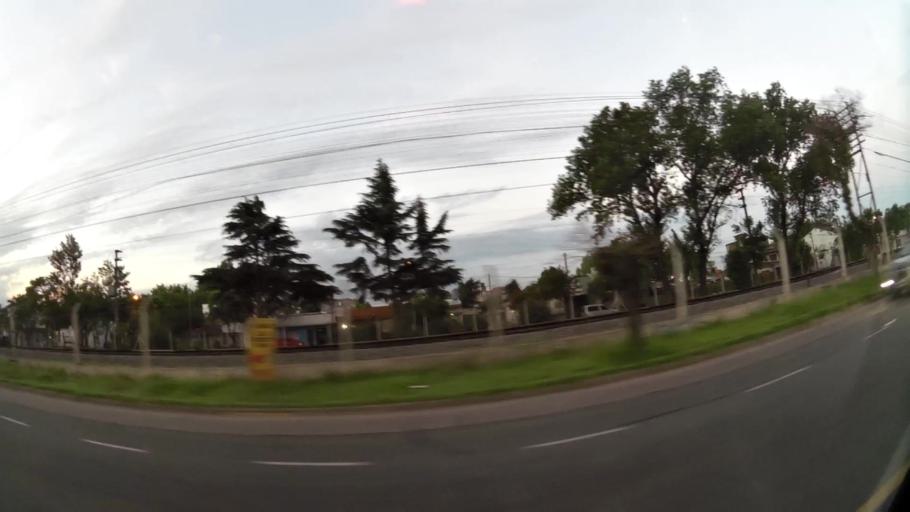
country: AR
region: Buenos Aires
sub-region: Partido de Merlo
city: Merlo
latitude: -34.6662
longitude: -58.7184
